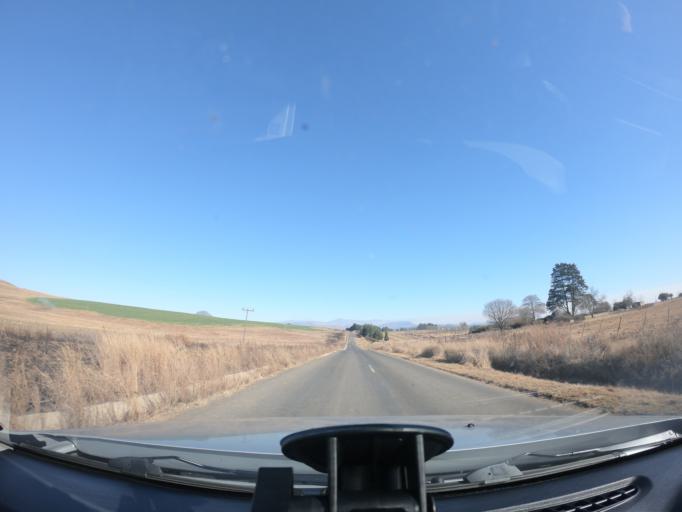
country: ZA
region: KwaZulu-Natal
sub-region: uMgungundlovu District Municipality
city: Mooirivier
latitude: -29.3256
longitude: 29.8622
